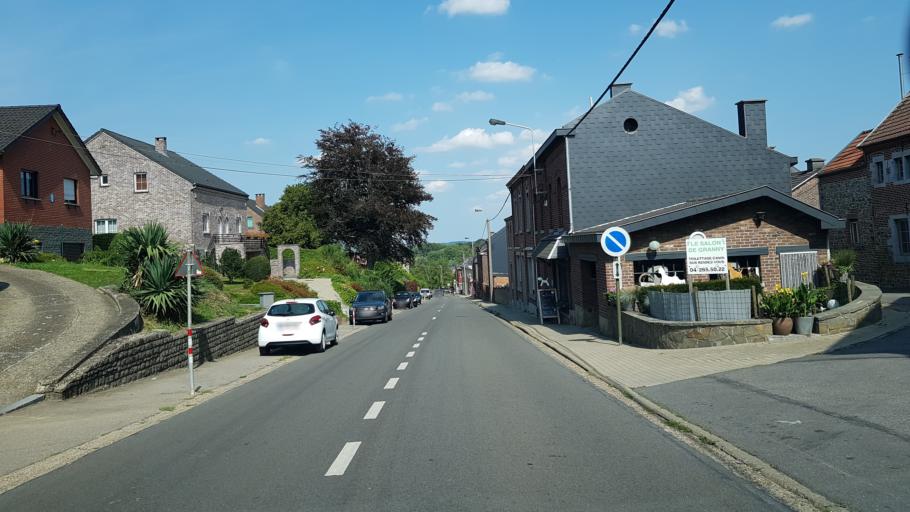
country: BE
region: Wallonia
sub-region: Province de Liege
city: Blegny
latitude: 50.6939
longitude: 5.6996
